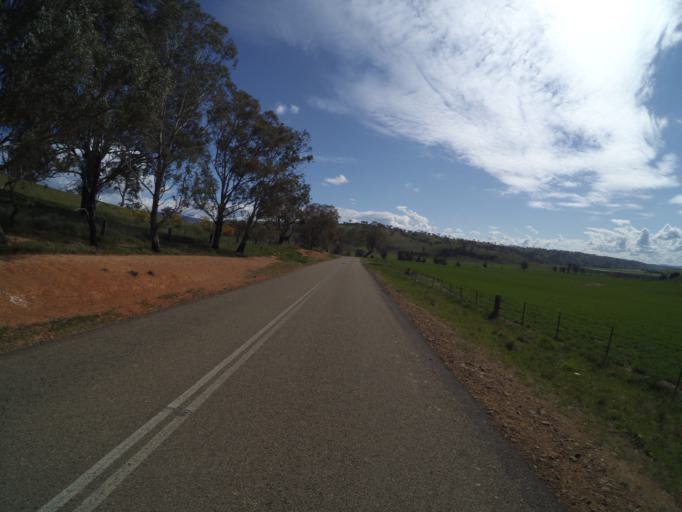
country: AU
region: New South Wales
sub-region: Yass Valley
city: Yass
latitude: -35.0202
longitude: 148.8447
